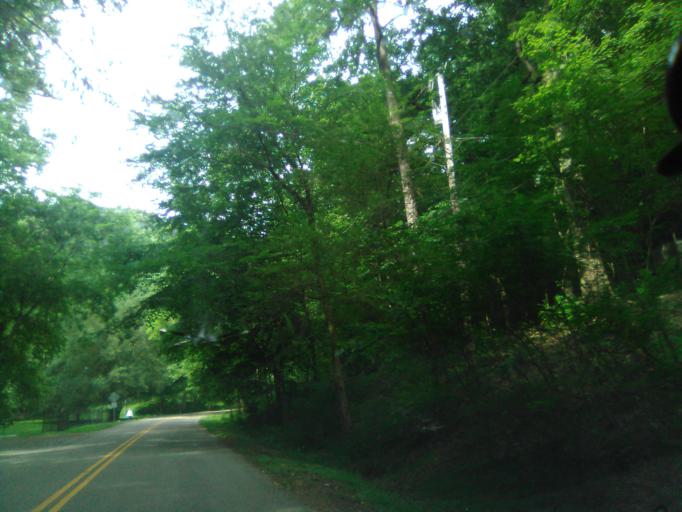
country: US
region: Tennessee
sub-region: Davidson County
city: Belle Meade
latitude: 36.0964
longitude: -86.9132
